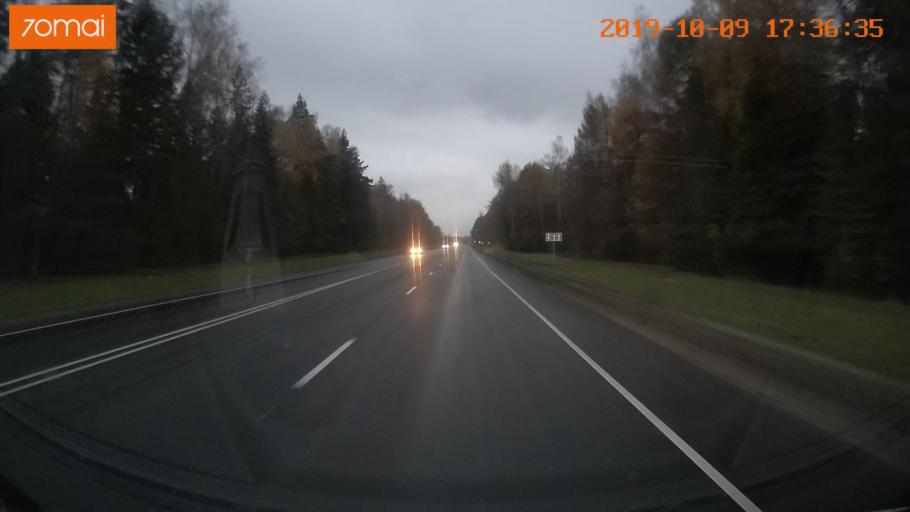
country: RU
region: Ivanovo
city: Bogorodskoye
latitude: 57.0763
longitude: 40.9953
